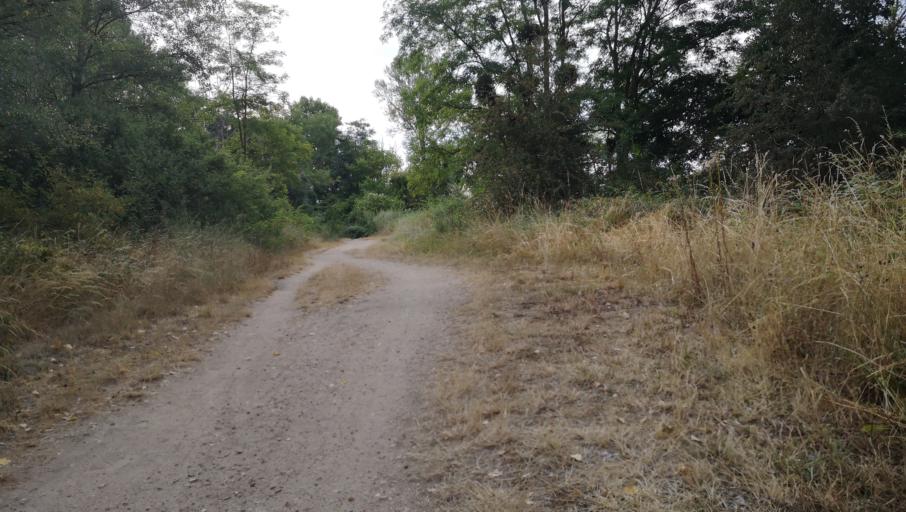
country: FR
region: Centre
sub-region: Departement du Loiret
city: Checy
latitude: 47.8891
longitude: 2.0063
